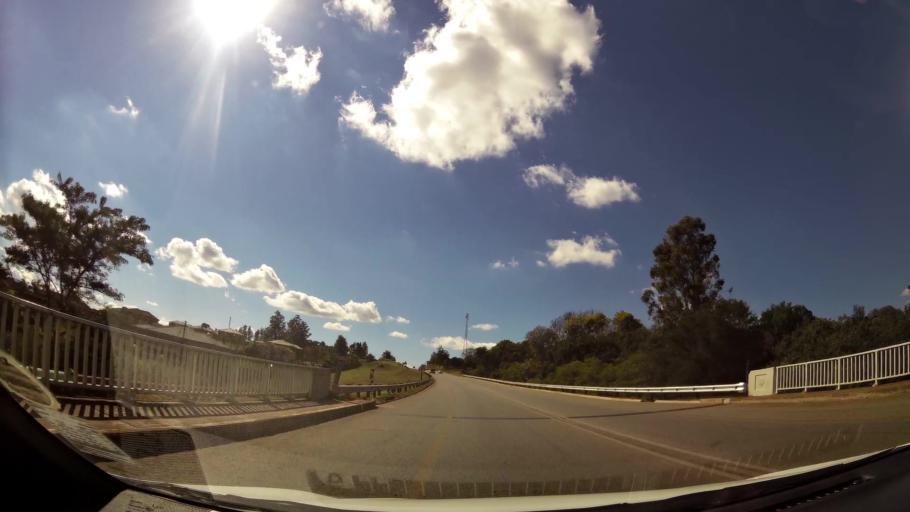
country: ZA
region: Limpopo
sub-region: Mopani District Municipality
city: Tzaneen
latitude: -23.8191
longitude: 30.1673
